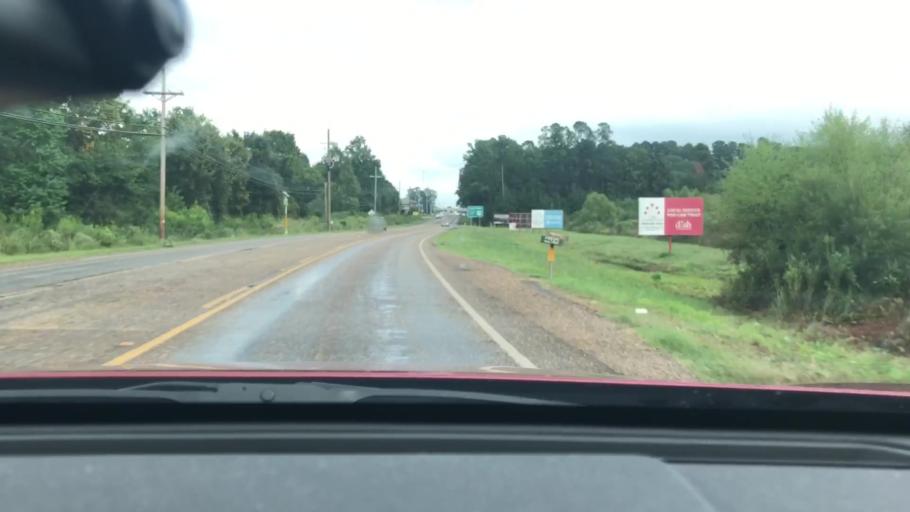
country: US
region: Texas
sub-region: Bowie County
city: Wake Village
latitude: 33.4436
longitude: -94.1070
